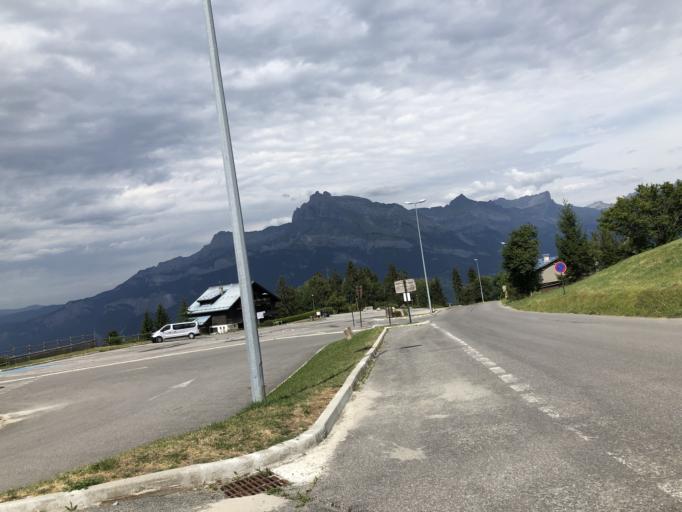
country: FR
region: Rhone-Alpes
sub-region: Departement de la Haute-Savoie
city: Combloux
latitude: 45.8927
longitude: 6.6257
